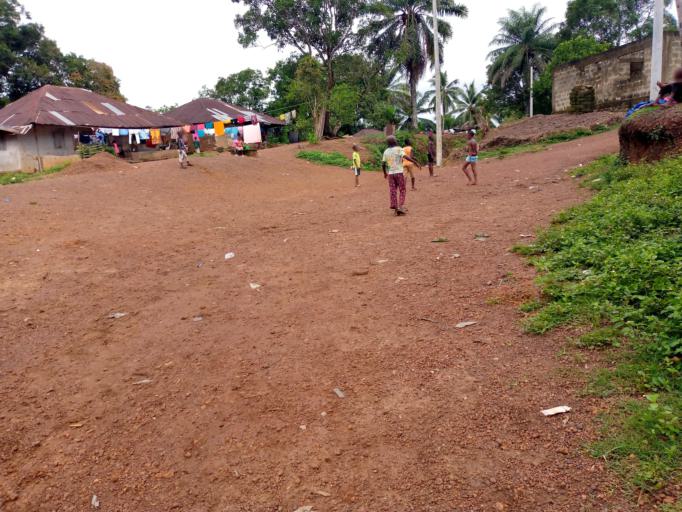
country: SL
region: Southern Province
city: Moyamba
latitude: 8.1578
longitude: -12.4320
